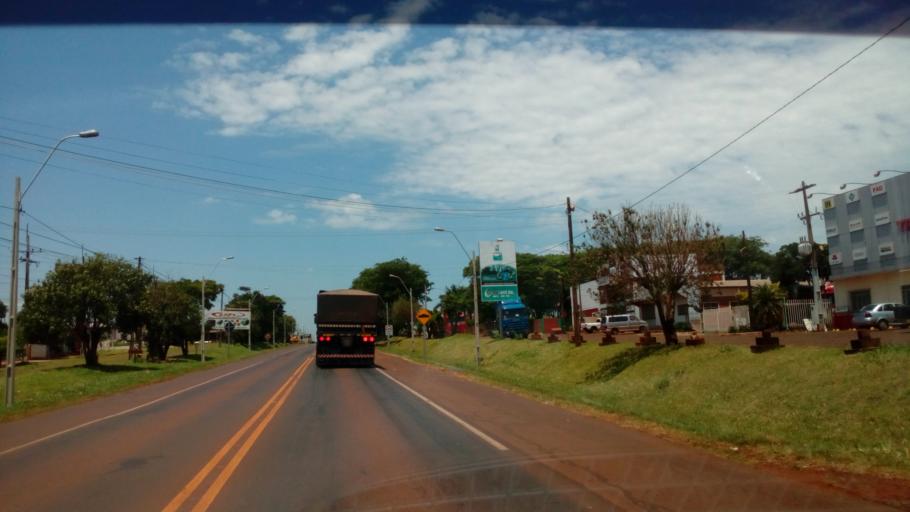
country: PY
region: Alto Parana
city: Santa Rita
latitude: -25.8148
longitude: -55.1069
